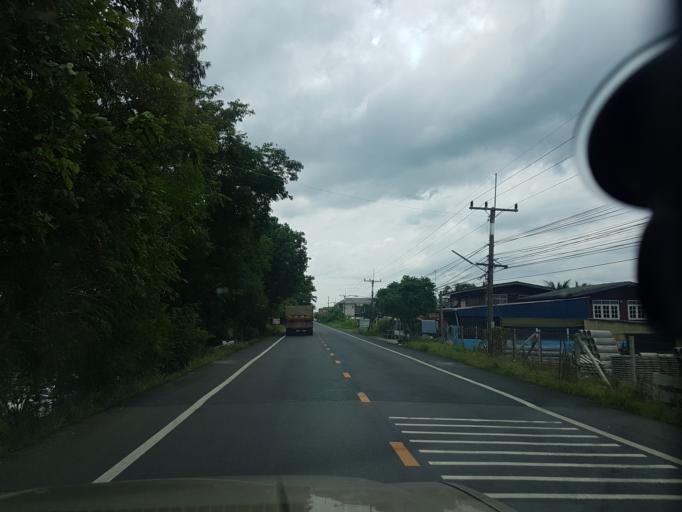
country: TH
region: Sara Buri
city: Nong Khae
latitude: 14.2803
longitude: 100.8918
